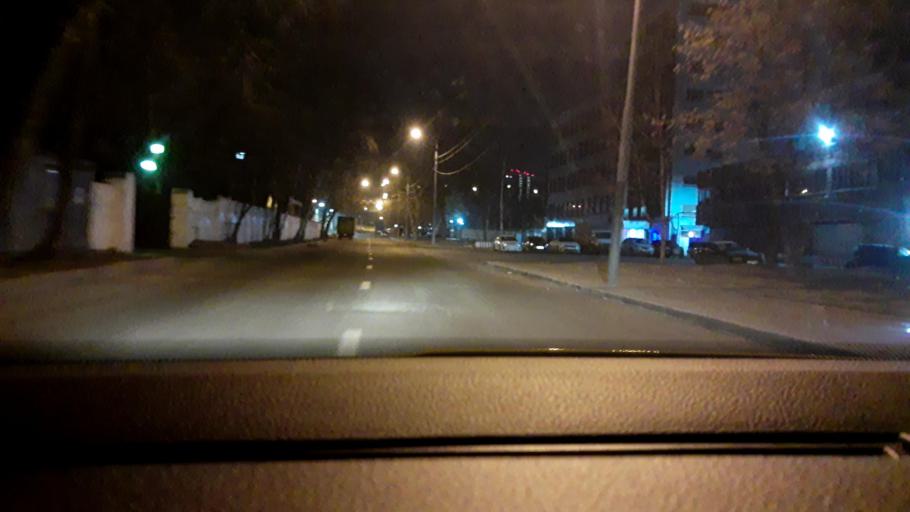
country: RU
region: Moscow
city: Zapadnoye Degunino
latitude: 55.8549
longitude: 37.5307
